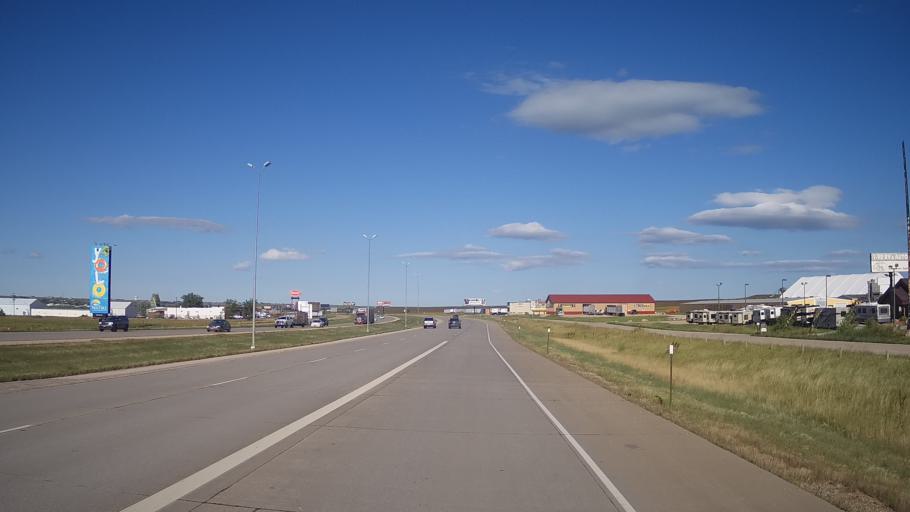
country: US
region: South Dakota
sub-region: Pennington County
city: Rapid Valley
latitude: 44.1004
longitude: -103.1443
